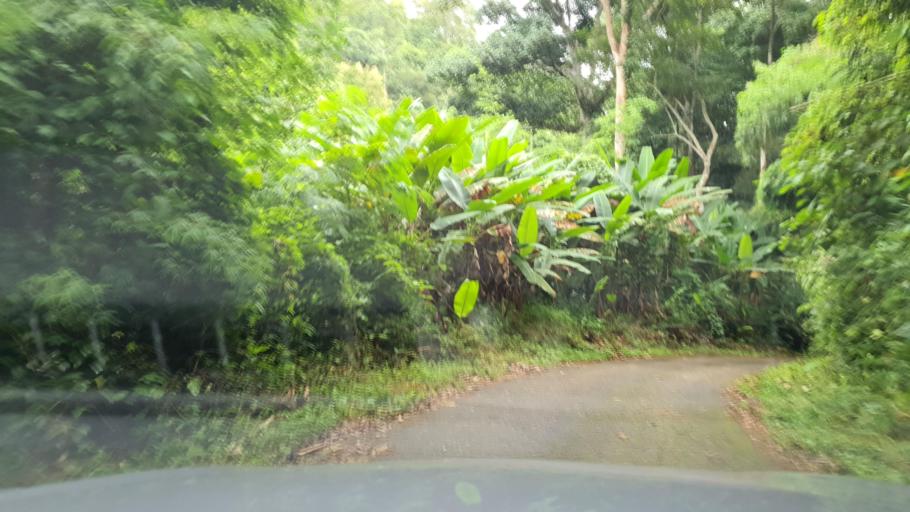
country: TH
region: Chiang Mai
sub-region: Amphoe Chiang Dao
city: Chiang Dao
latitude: 19.2747
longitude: 98.9522
